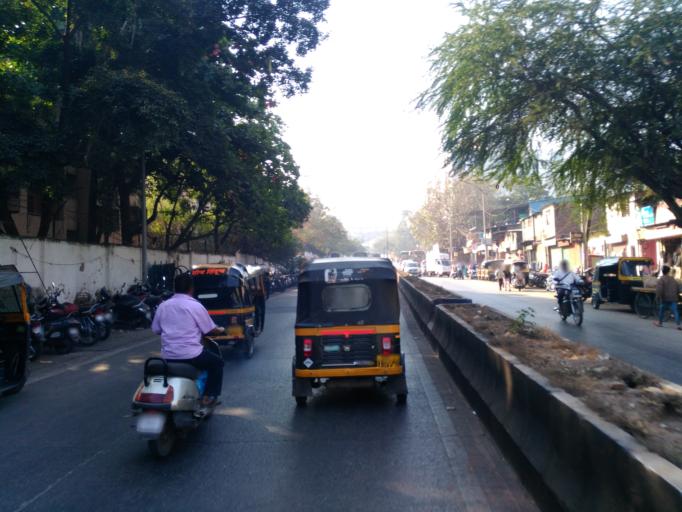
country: IN
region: Maharashtra
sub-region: Pune Division
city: Pune
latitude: 18.4943
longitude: 73.8693
